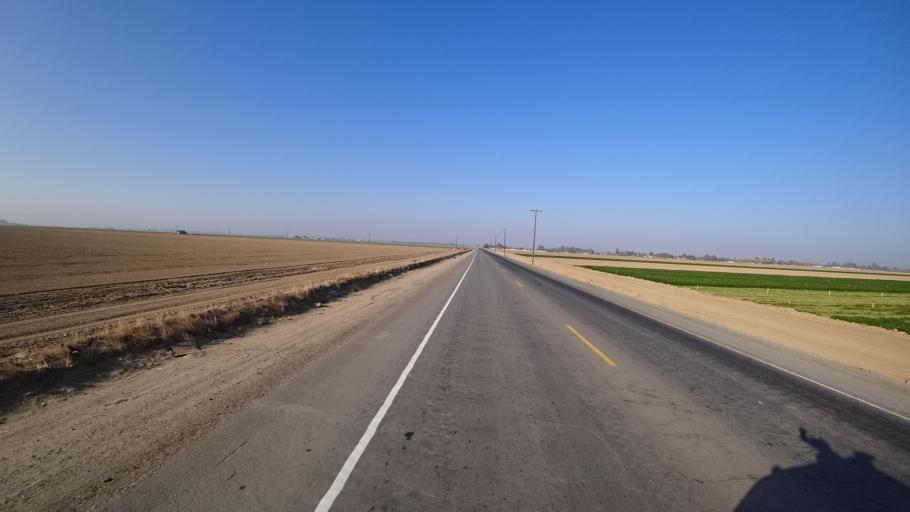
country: US
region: California
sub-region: Kern County
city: Weedpatch
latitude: 35.2378
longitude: -118.9506
